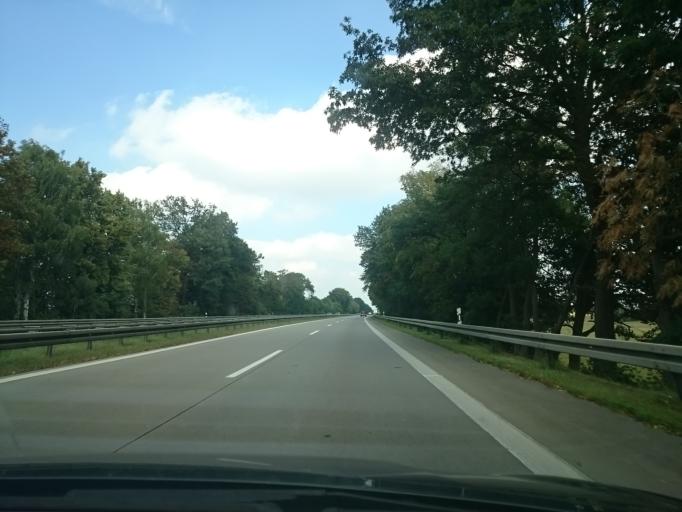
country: DE
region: Brandenburg
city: Marienwerder
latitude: 52.8631
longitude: 13.6778
